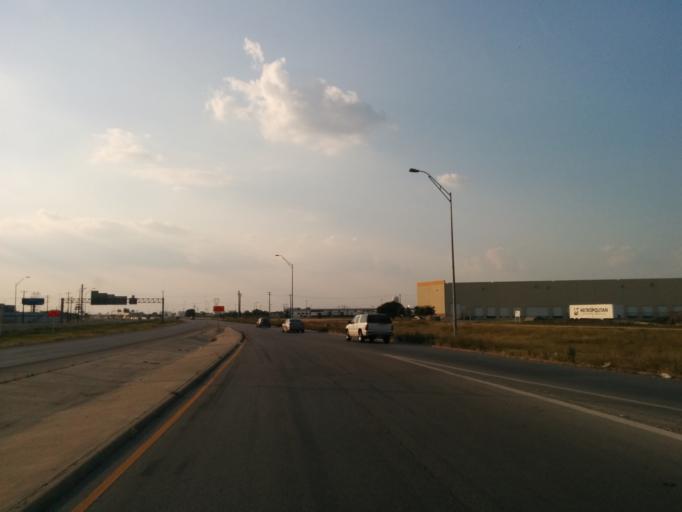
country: US
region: Texas
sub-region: Bexar County
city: Kirby
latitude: 29.4386
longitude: -98.3911
